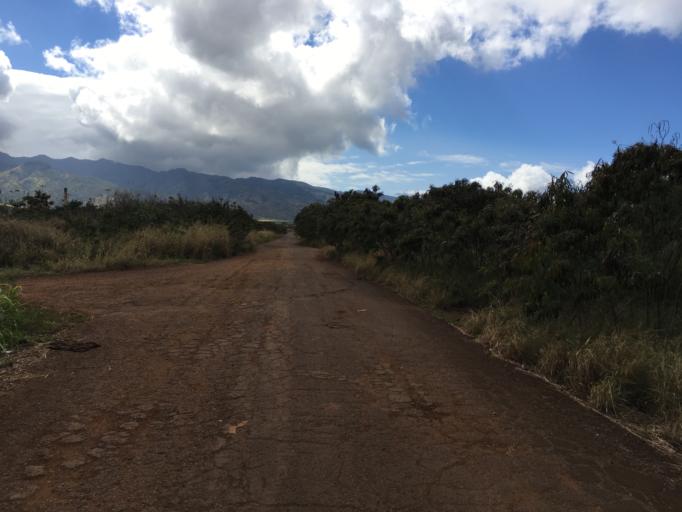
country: US
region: Hawaii
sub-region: Honolulu County
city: Waialua
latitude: 21.5806
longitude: -158.1200
